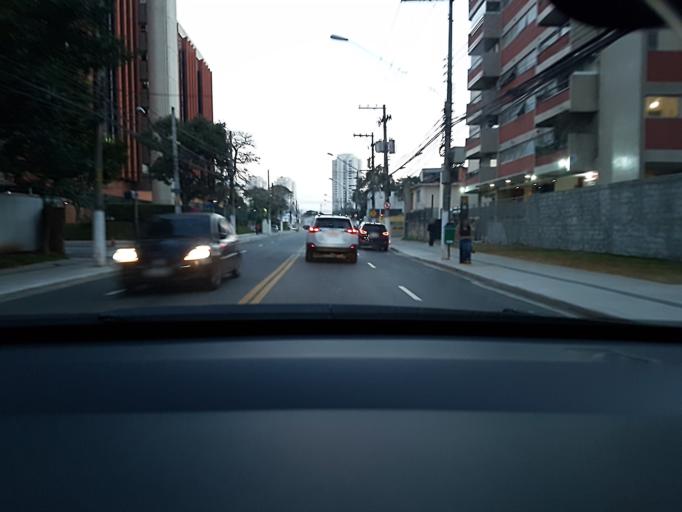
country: BR
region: Sao Paulo
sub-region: Taboao Da Serra
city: Taboao da Serra
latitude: -23.6321
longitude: -46.7107
